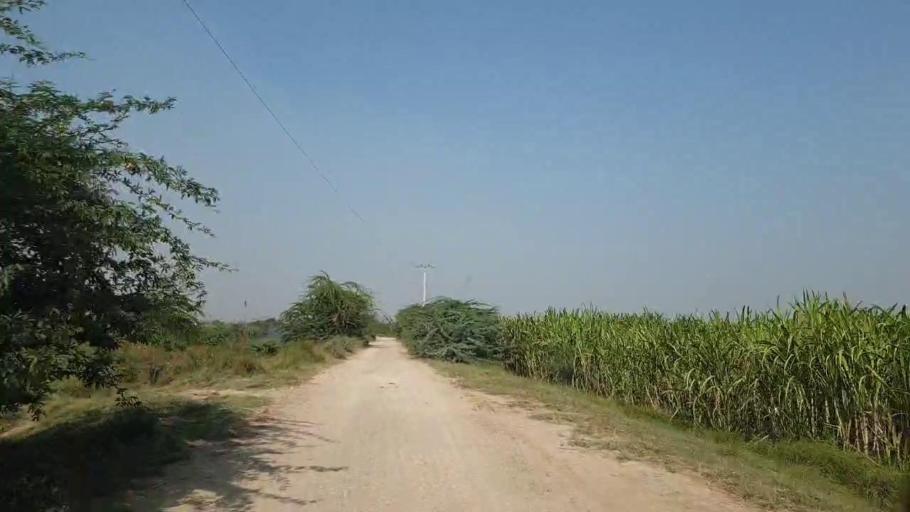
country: PK
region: Sindh
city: Bulri
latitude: 24.9382
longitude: 68.3858
